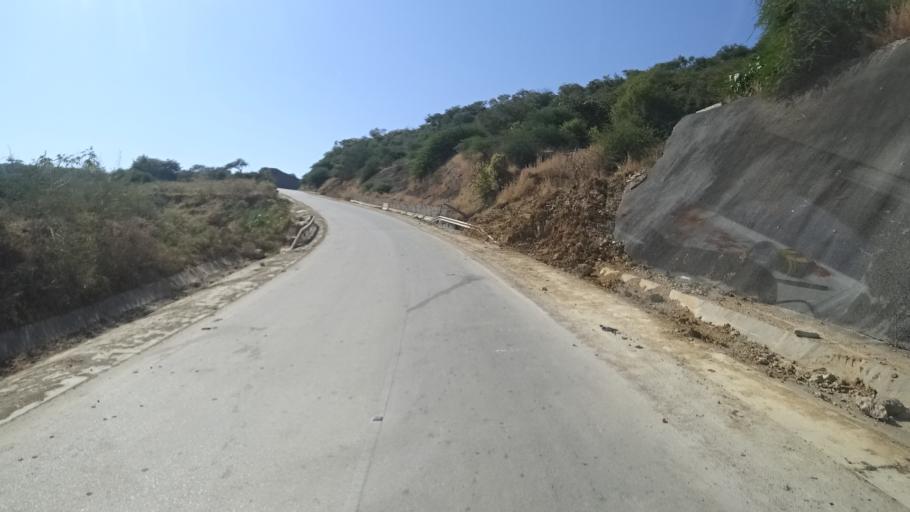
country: OM
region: Zufar
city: Salalah
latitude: 17.0612
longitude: 54.6089
